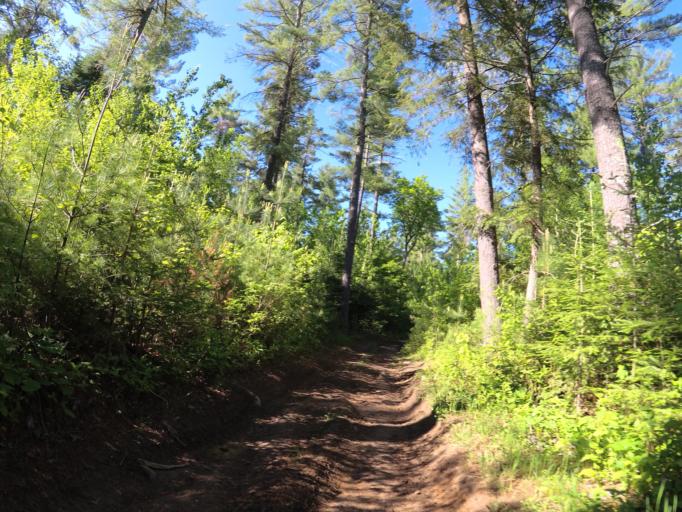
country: CA
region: Ontario
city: Renfrew
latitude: 45.1209
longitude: -77.0279
